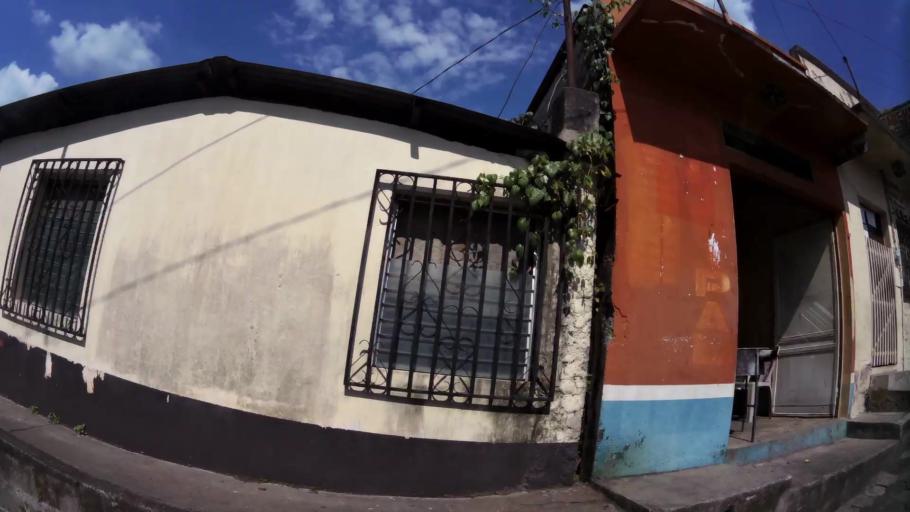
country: GT
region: Suchitepeque
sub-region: Municipio de Cuyotenango
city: Cuyotenango
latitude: 14.5396
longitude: -91.5723
